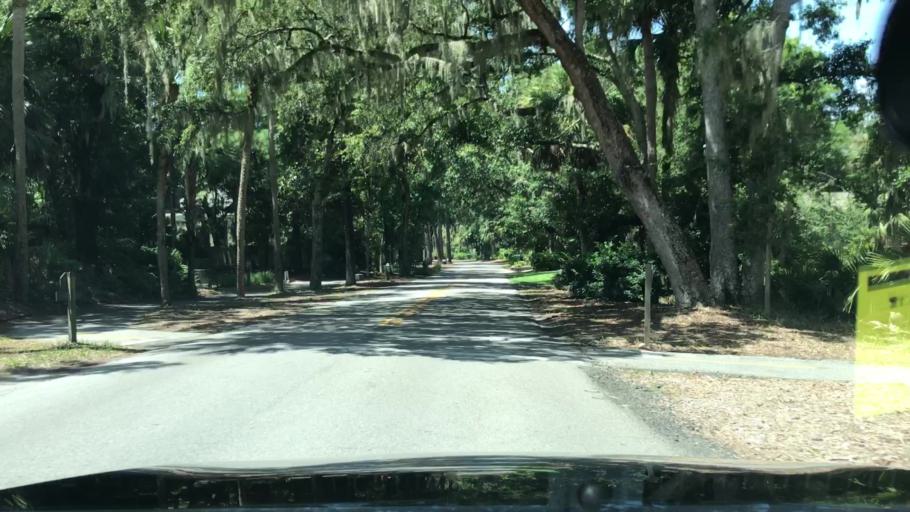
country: US
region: South Carolina
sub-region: Beaufort County
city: Hilton Head Island
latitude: 32.1307
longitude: -80.7800
